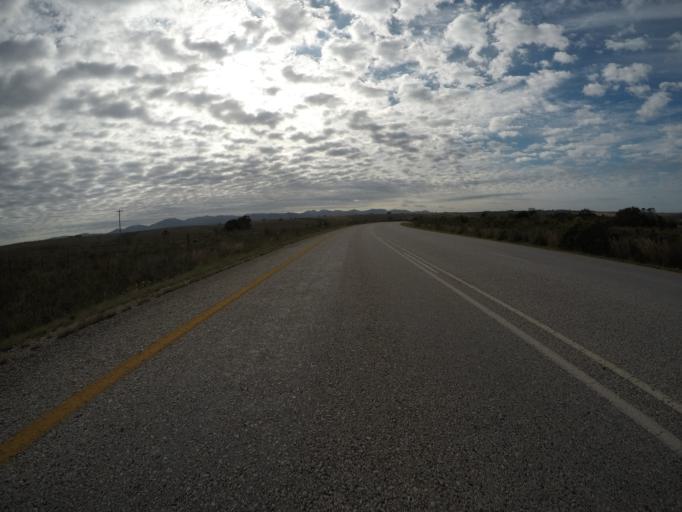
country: ZA
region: Eastern Cape
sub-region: Cacadu District Municipality
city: Kruisfontein
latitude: -34.0326
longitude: 24.5542
